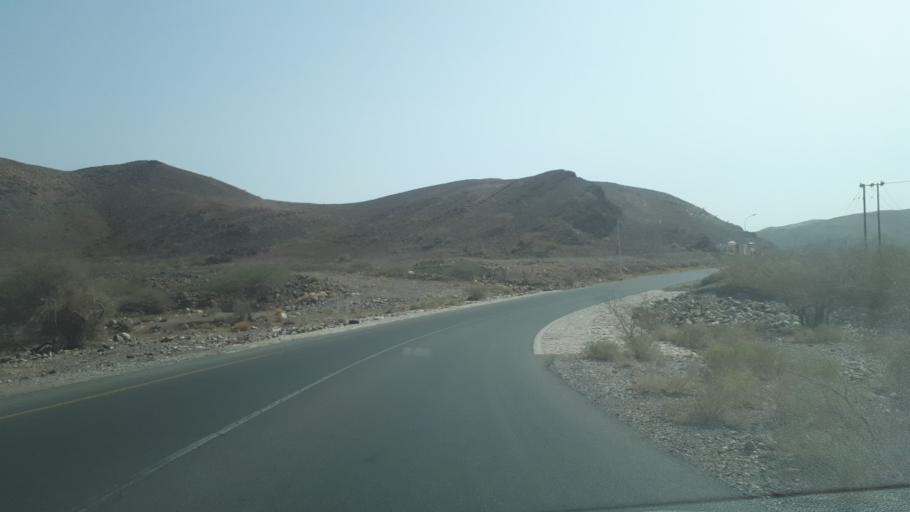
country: OM
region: Muhafazat ad Dakhiliyah
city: Bahla'
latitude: 23.2039
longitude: 56.9509
